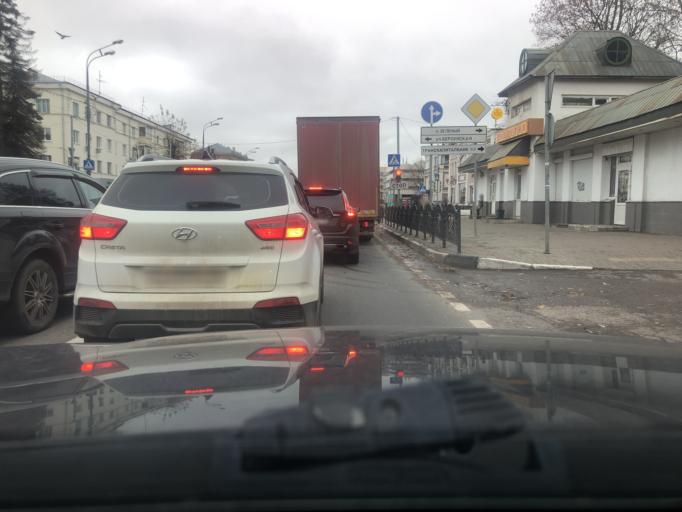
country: RU
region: Moskovskaya
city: Sergiyev Posad
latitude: 56.3181
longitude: 38.1390
